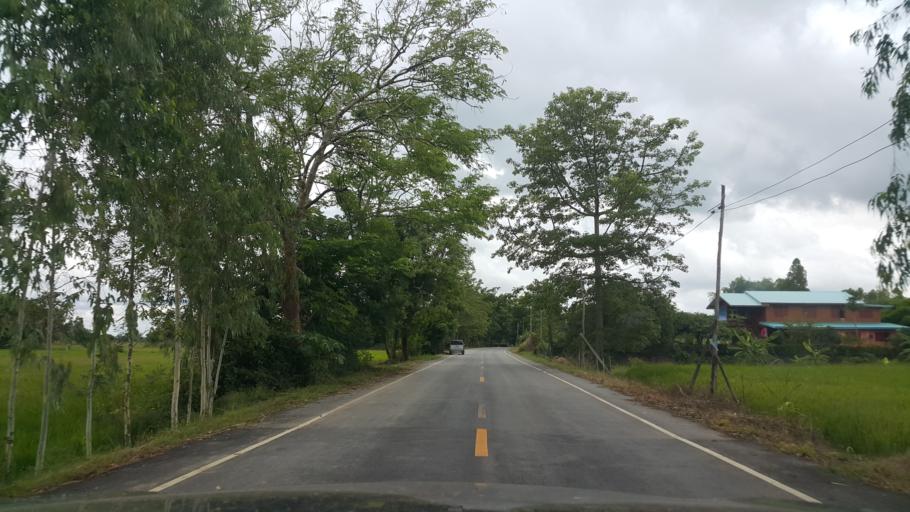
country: TH
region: Sukhothai
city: Kong Krailat
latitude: 16.9135
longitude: 99.8866
